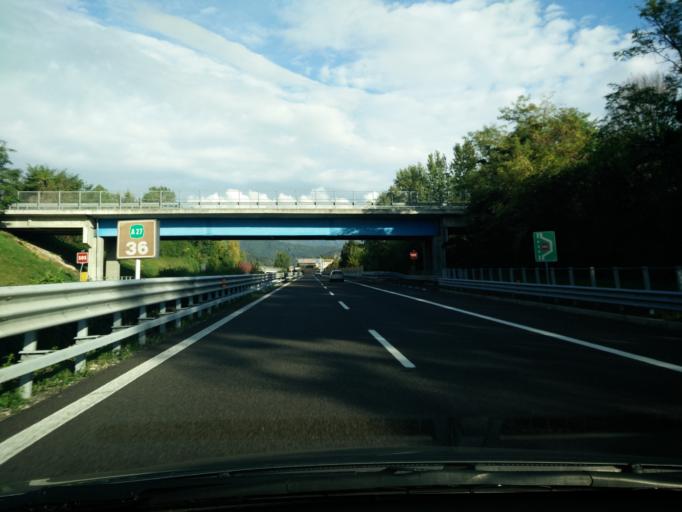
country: IT
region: Veneto
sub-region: Provincia di Treviso
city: Carpesica
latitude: 45.9545
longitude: 12.2927
